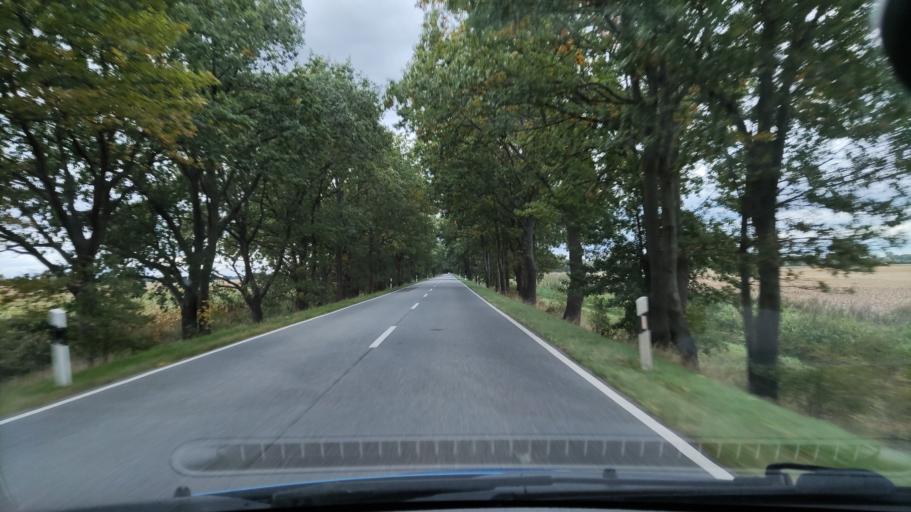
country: DE
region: Lower Saxony
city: Neu Darchau
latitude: 53.3248
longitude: 10.9501
